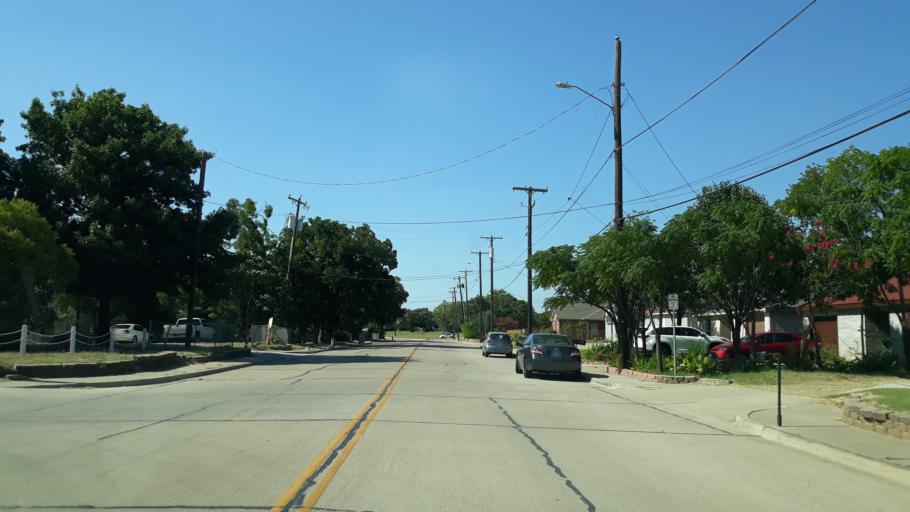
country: US
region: Texas
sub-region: Dallas County
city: Irving
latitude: 32.8197
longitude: -97.0039
